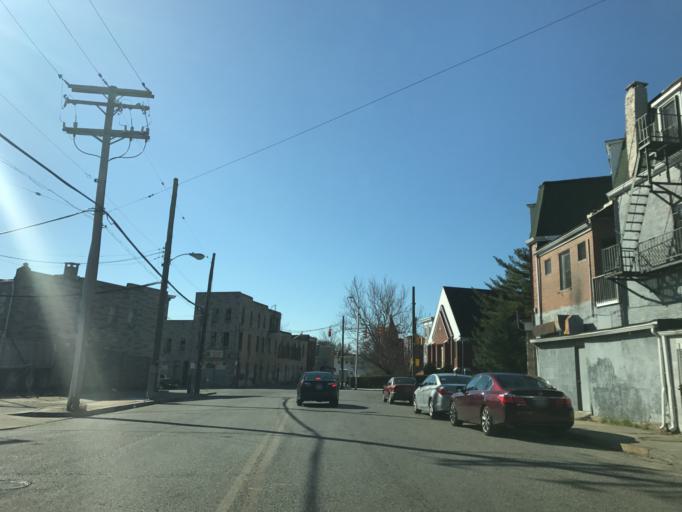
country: US
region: Maryland
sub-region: Baltimore County
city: Lansdowne
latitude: 39.2881
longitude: -76.6592
